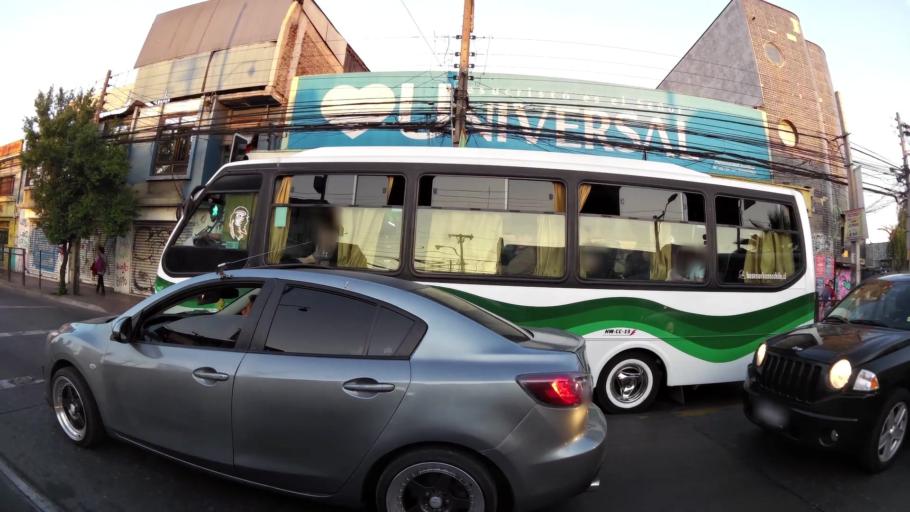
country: CL
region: Santiago Metropolitan
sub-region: Provincia de Santiago
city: Santiago
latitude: -33.5170
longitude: -70.6587
